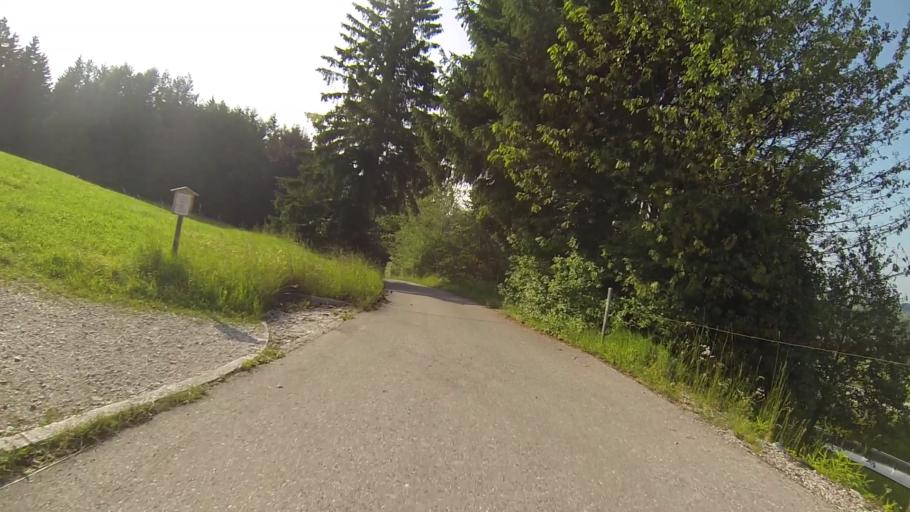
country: DE
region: Bavaria
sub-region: Swabia
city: Nesselwang
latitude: 47.6156
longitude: 10.4963
